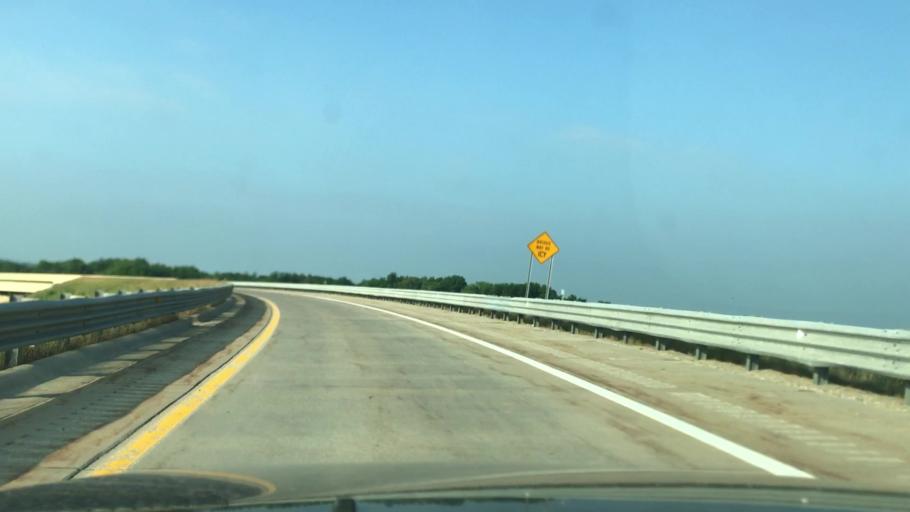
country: US
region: Michigan
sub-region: Ottawa County
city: Hudsonville
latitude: 42.8621
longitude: -85.8161
